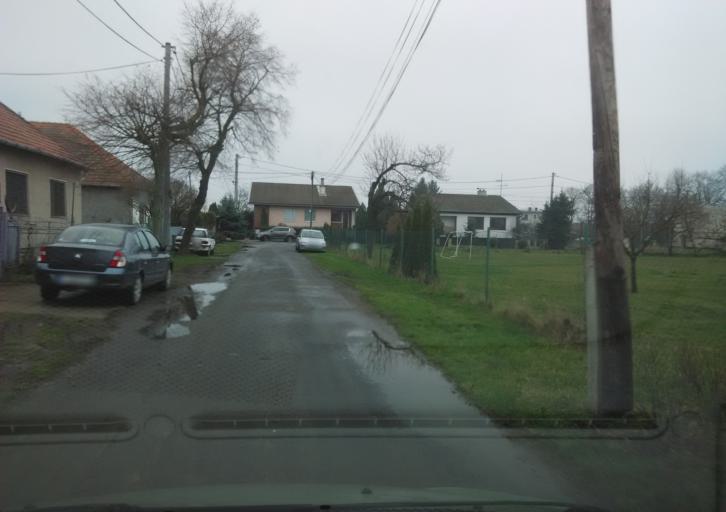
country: SK
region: Nitriansky
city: Tlmace
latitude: 48.2753
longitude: 18.5421
